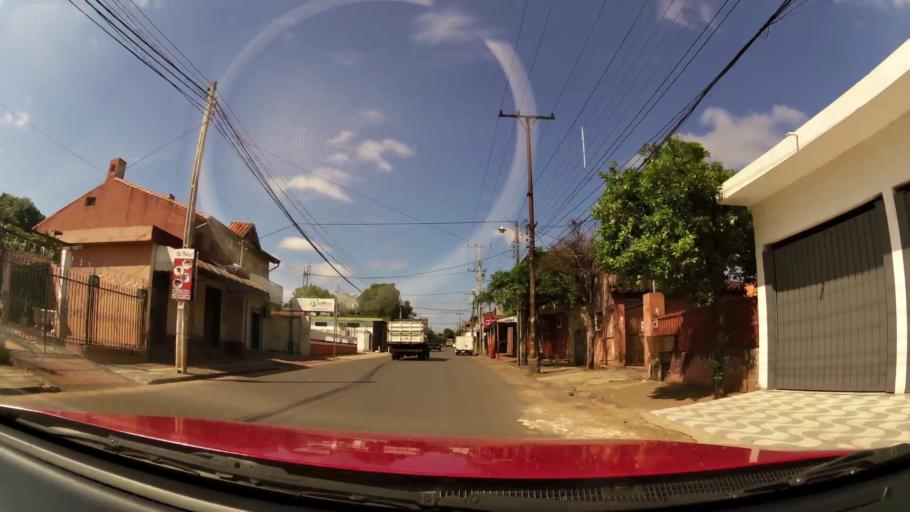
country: PY
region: Central
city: San Lorenzo
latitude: -25.2585
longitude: -57.4899
